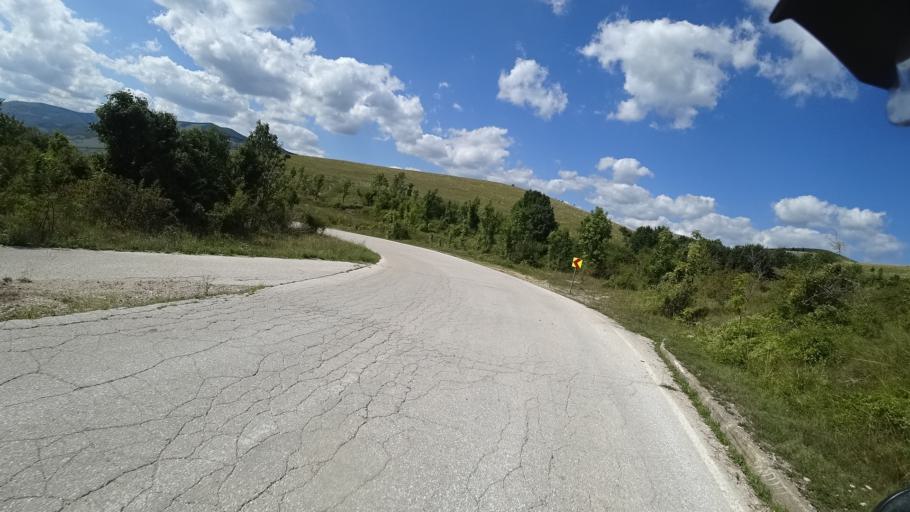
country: BA
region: Federation of Bosnia and Herzegovina
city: Orasac
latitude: 44.4661
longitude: 15.9793
